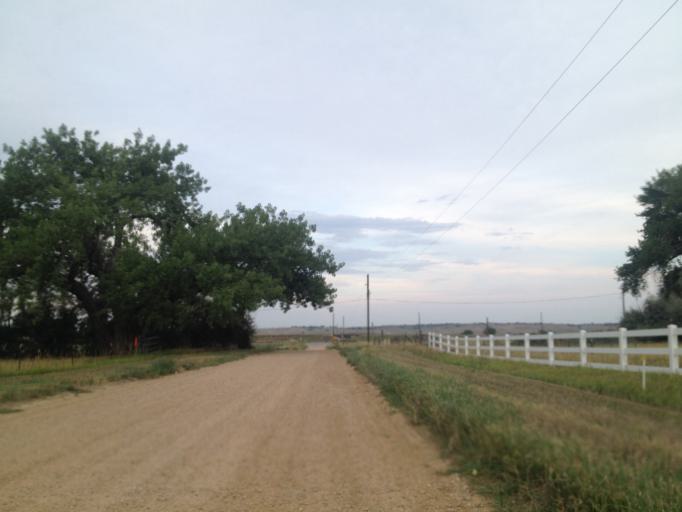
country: US
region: Colorado
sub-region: Boulder County
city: Louisville
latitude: 39.9524
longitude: -105.1317
